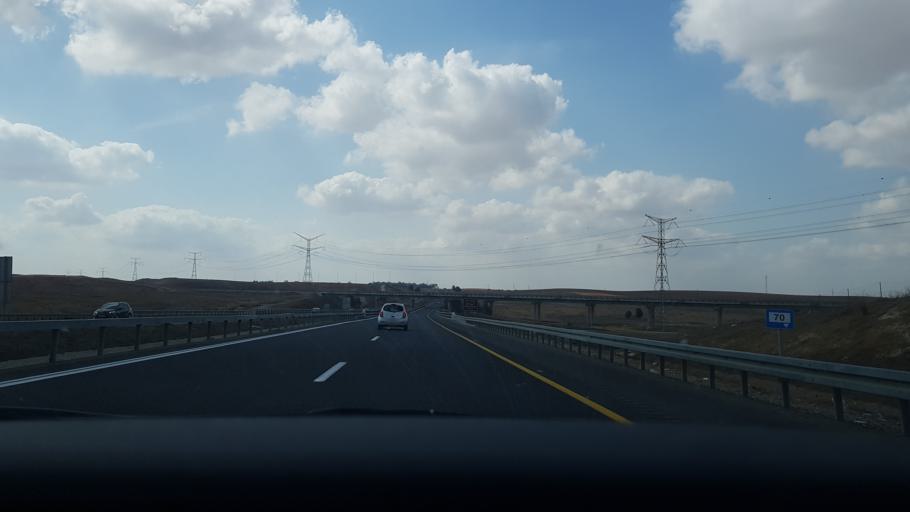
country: IL
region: Southern District
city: Qiryat Gat
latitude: 31.5290
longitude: 34.7911
